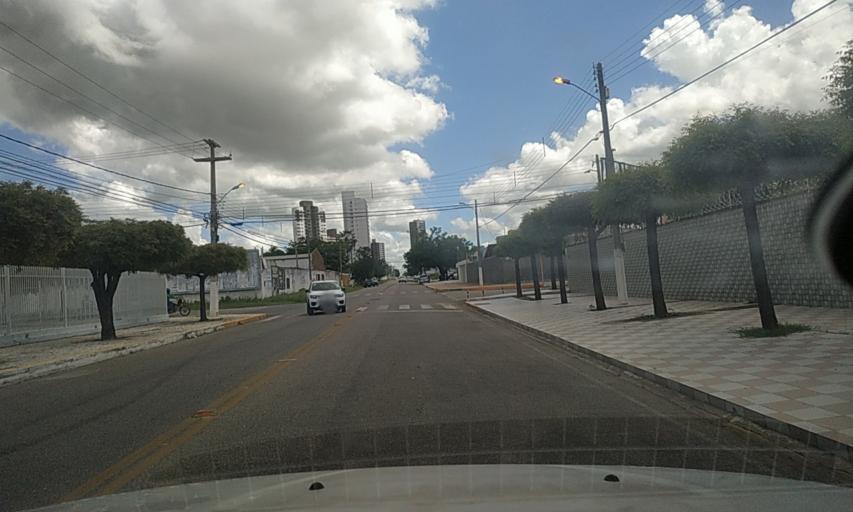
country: BR
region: Rio Grande do Norte
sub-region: Mossoro
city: Mossoro
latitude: -5.1828
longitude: -37.3557
